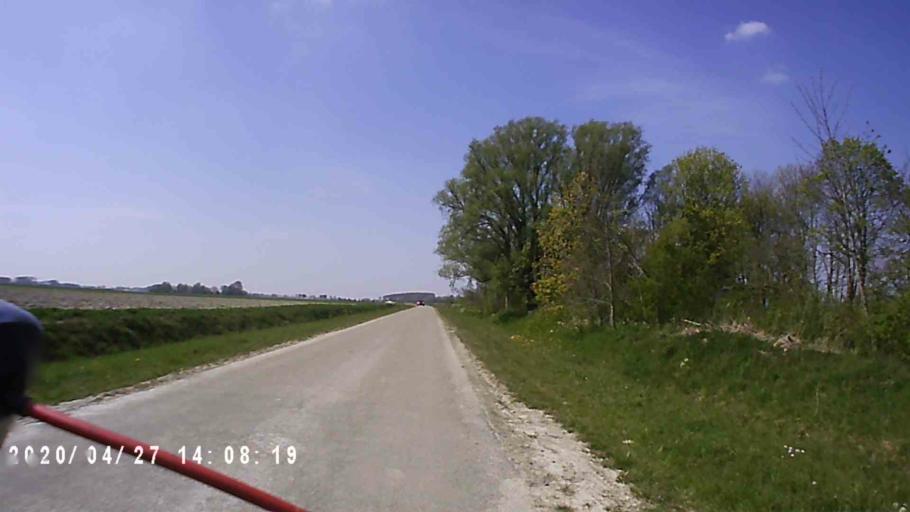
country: NL
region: Groningen
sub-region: Gemeente Zuidhorn
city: Oldehove
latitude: 53.3458
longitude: 6.3936
